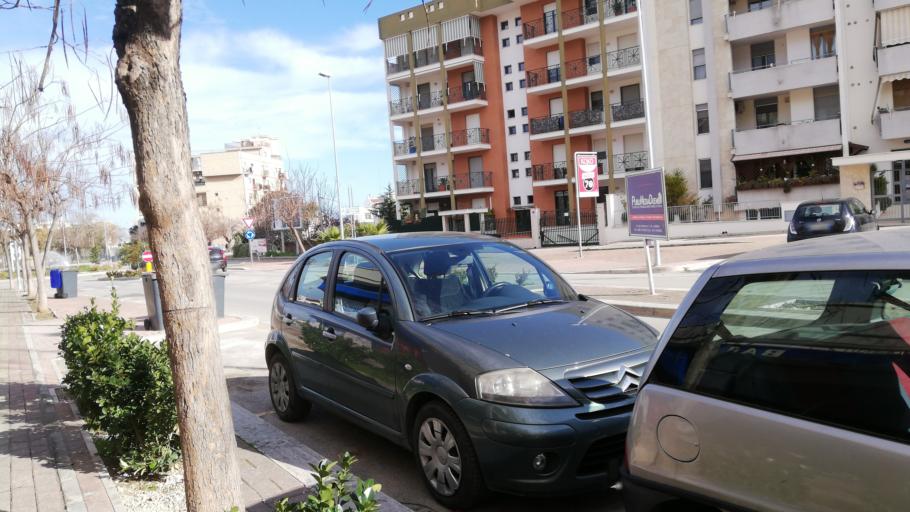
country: IT
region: Apulia
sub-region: Provincia di Barletta - Andria - Trani
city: Andria
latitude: 41.2363
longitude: 16.3032
